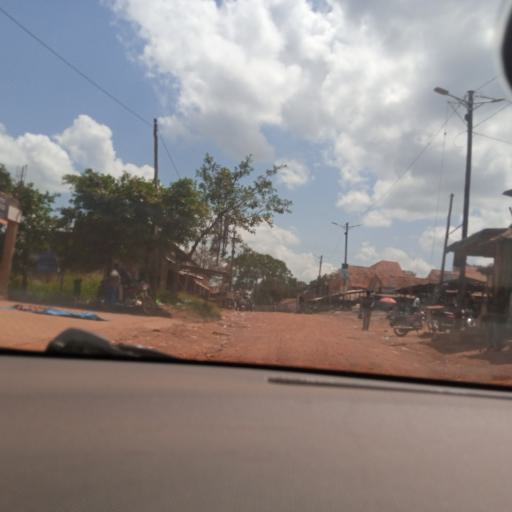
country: UG
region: Central Region
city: Masaka
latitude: -0.3297
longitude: 31.7393
